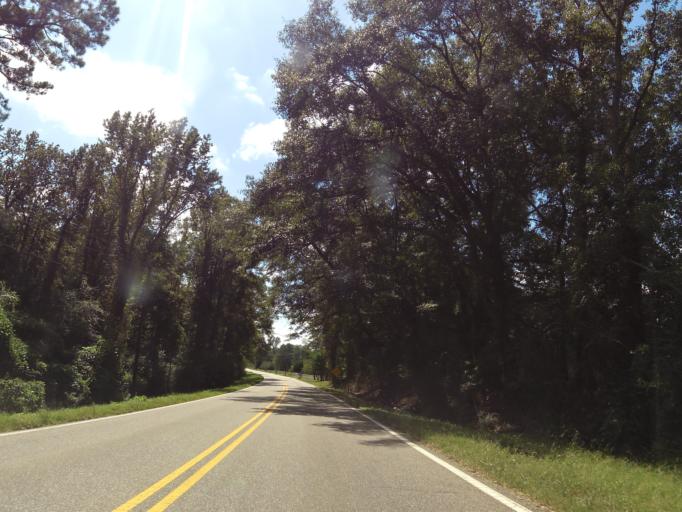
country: US
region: Alabama
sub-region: Dallas County
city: Selma
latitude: 32.4016
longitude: -87.0875
